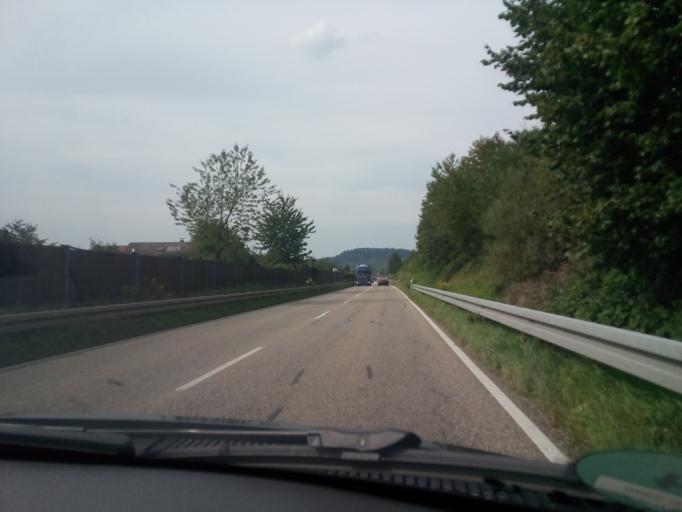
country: DE
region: Baden-Wuerttemberg
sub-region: Freiburg Region
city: Kappelrodeck
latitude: 48.5884
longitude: 8.1247
